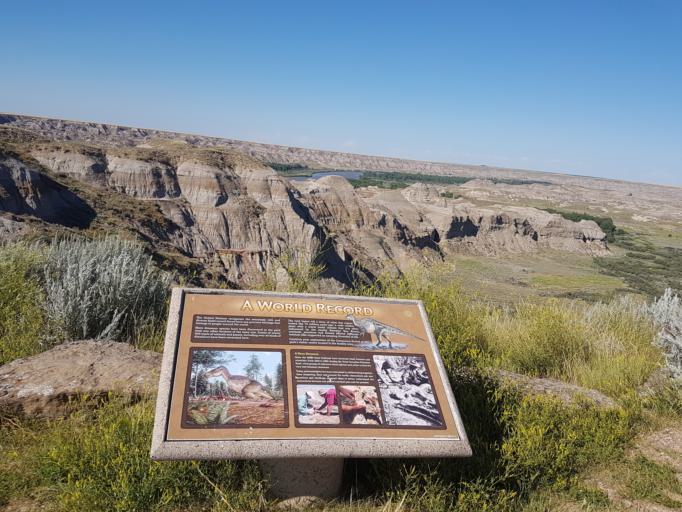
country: CA
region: Alberta
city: Brooks
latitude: 50.7529
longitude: -111.5263
